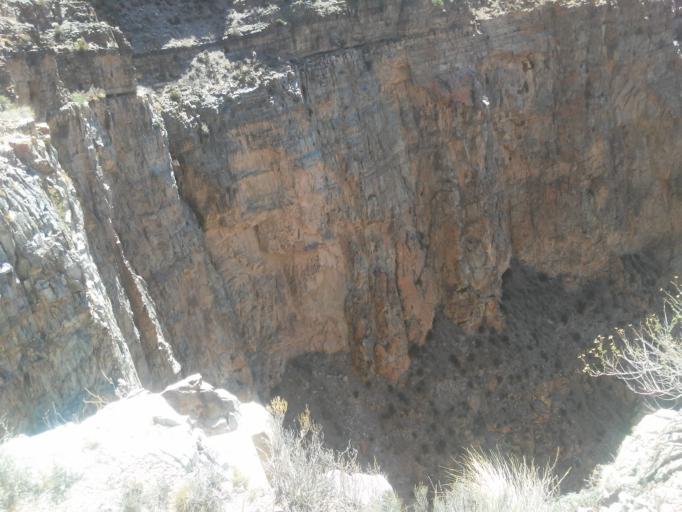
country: AR
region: Mendoza
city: Las Heras
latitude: -32.4813
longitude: -69.0737
